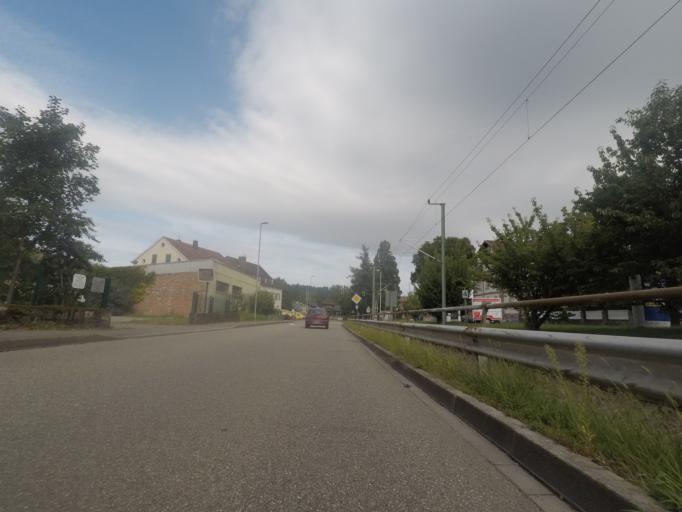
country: DE
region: Baden-Wuerttemberg
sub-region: Karlsruhe Region
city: Gernsbach
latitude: 48.7663
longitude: 8.3367
